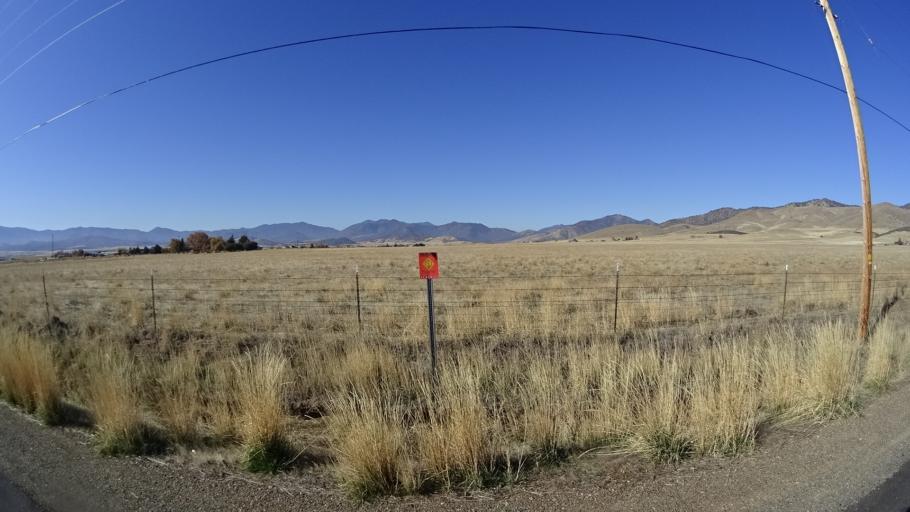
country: US
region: California
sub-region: Siskiyou County
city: Montague
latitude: 41.7636
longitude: -122.5231
